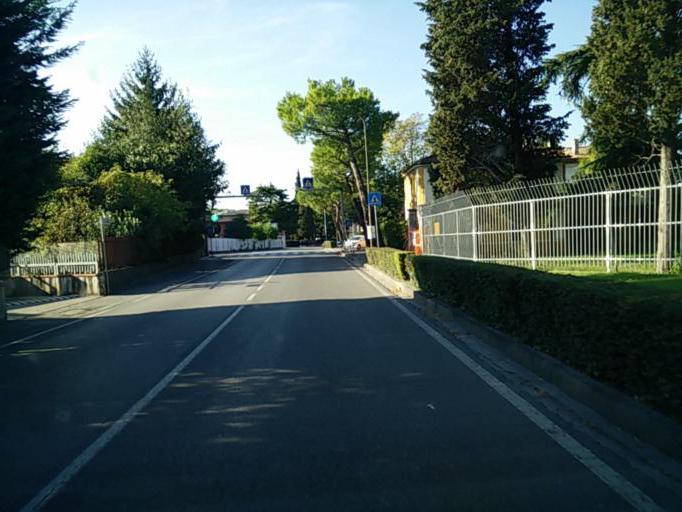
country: IT
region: Lombardy
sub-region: Provincia di Brescia
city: Desenzano del Garda
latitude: 45.4638
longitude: 10.5532
